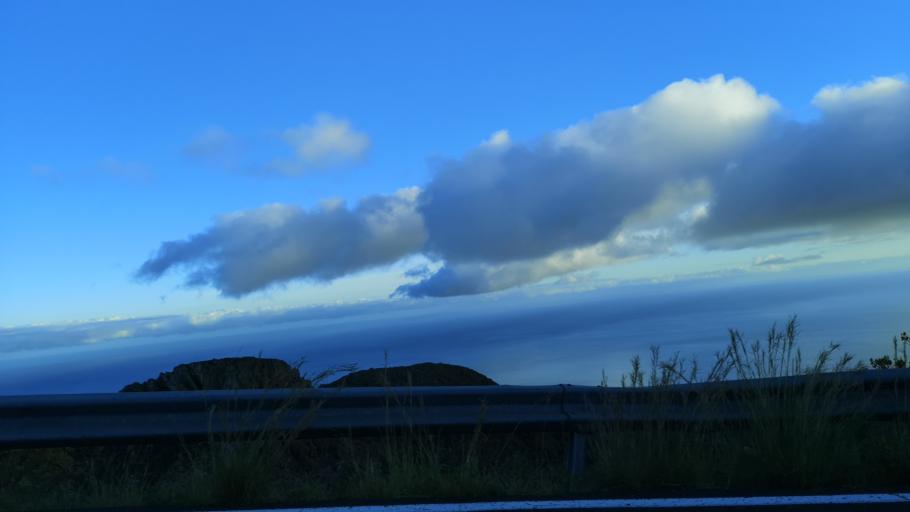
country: ES
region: Canary Islands
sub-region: Provincia de Santa Cruz de Tenerife
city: Alajero
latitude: 28.0566
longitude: -17.2279
